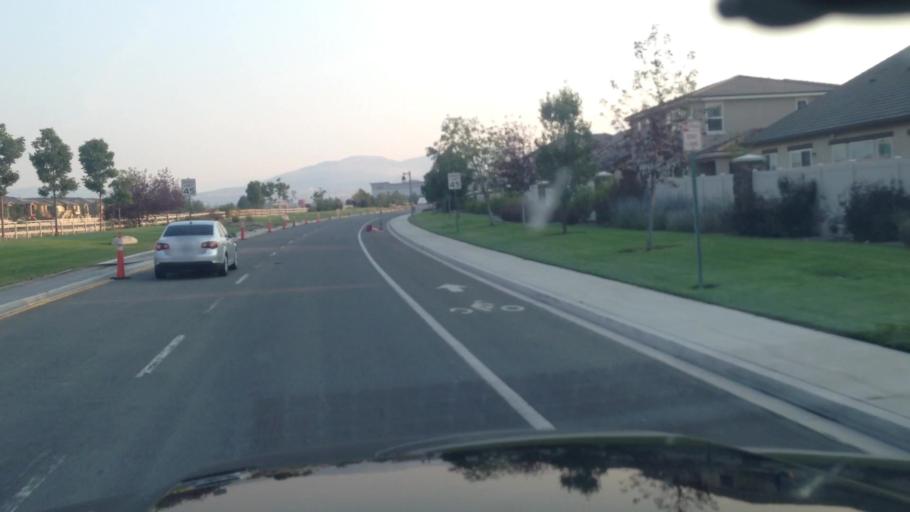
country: US
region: Nevada
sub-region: Washoe County
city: Sparks
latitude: 39.4291
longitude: -119.7309
